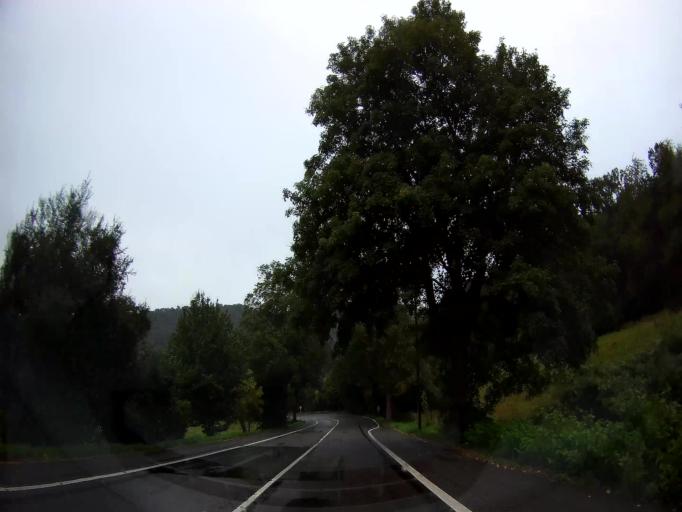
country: BE
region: Wallonia
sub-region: Province de Liege
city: Pepinster
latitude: 50.5655
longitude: 5.7847
